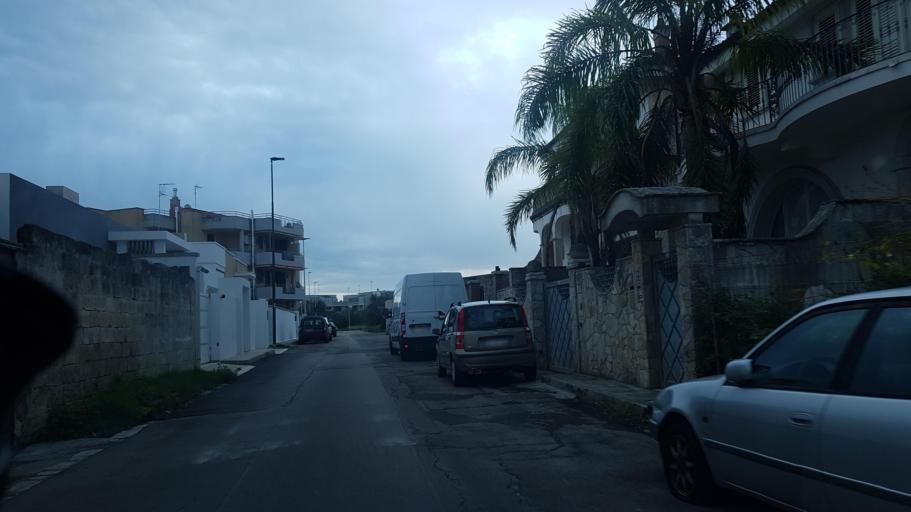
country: IT
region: Apulia
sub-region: Provincia di Lecce
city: Merine
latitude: 40.3343
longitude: 18.2213
